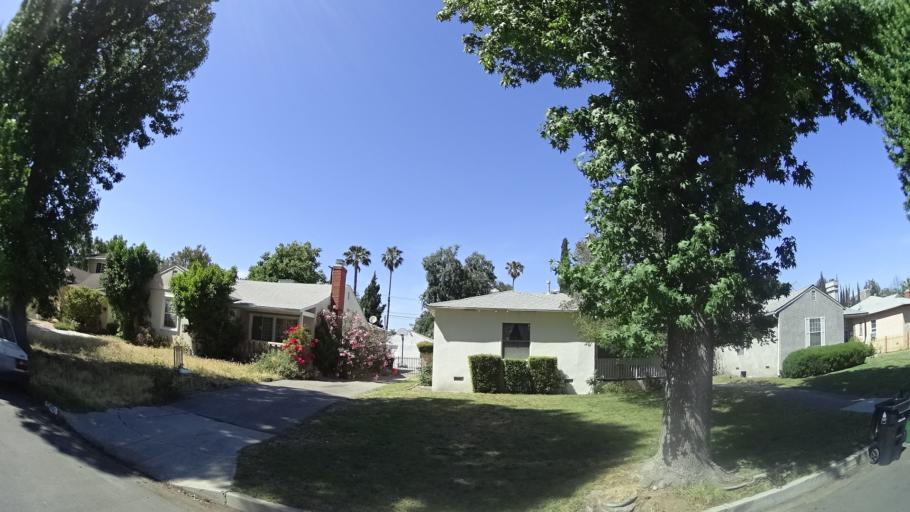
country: US
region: California
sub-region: Los Angeles County
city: North Hollywood
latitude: 34.1776
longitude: -118.4078
